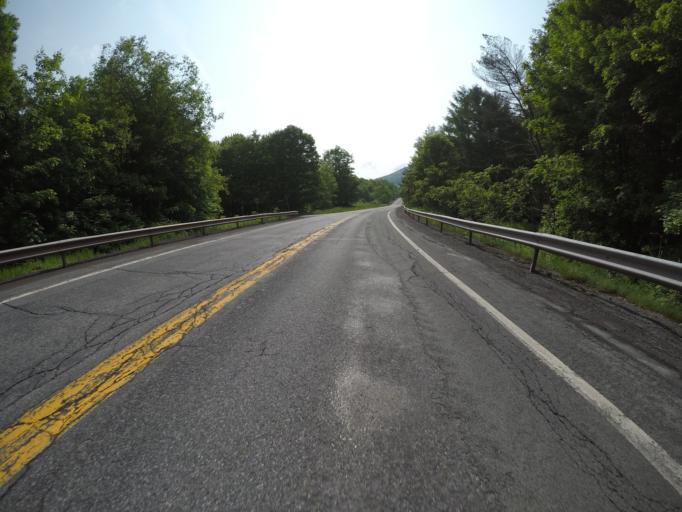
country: US
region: New York
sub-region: Delaware County
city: Delhi
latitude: 42.1213
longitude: -74.7390
